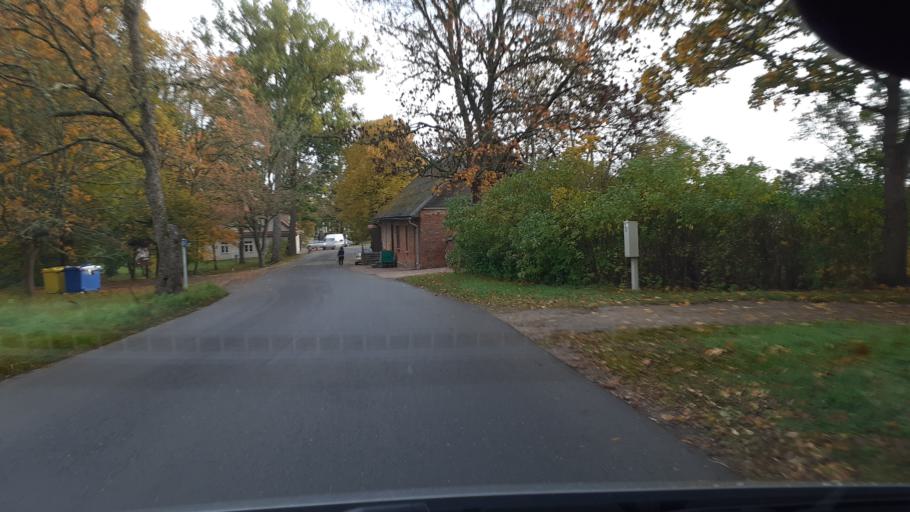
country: LV
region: Kuldigas Rajons
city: Kuldiga
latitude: 57.0155
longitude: 21.9115
